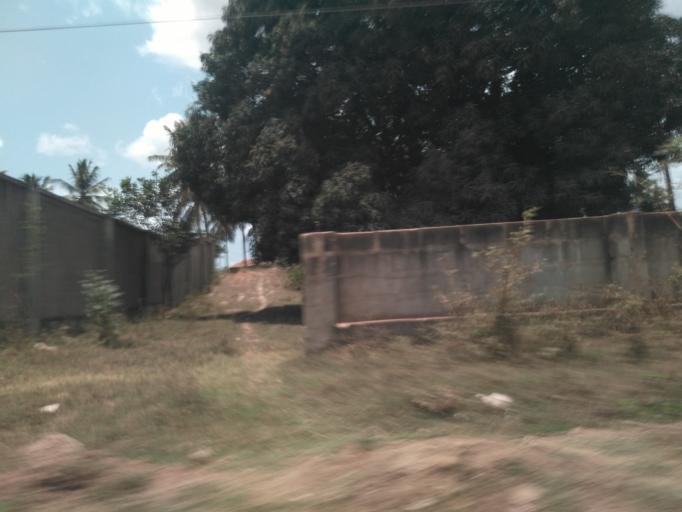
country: TZ
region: Dar es Salaam
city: Dar es Salaam
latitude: -6.8402
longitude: 39.3308
